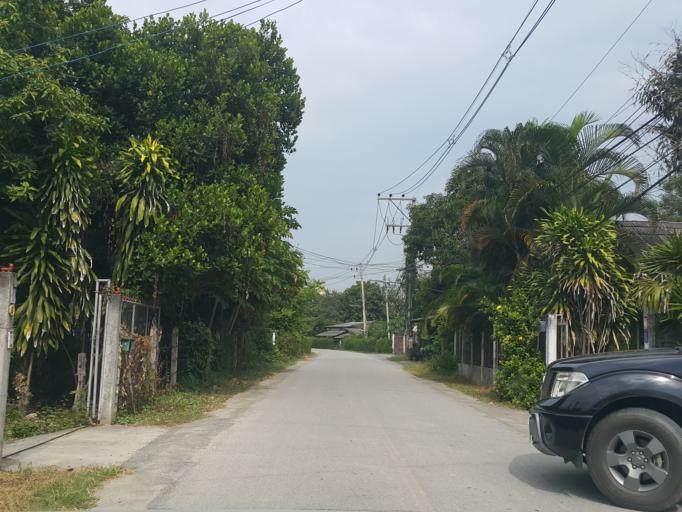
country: TH
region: Chiang Mai
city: San Kamphaeng
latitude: 18.8032
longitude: 99.0993
